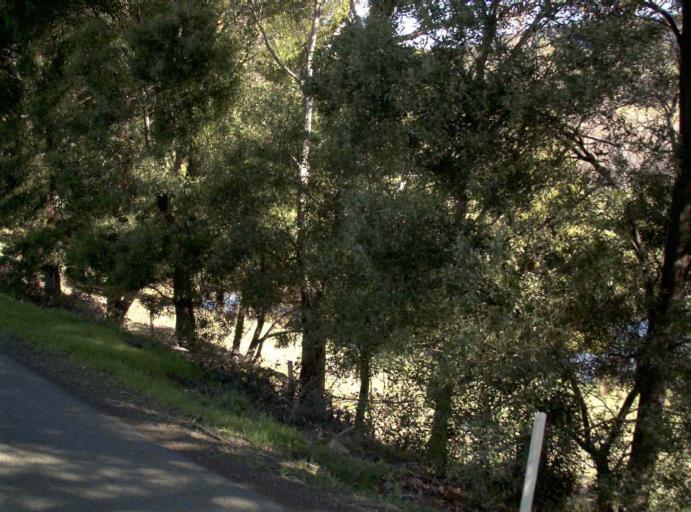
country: AU
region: Tasmania
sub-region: Launceston
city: Mayfield
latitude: -41.2578
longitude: 147.1371
